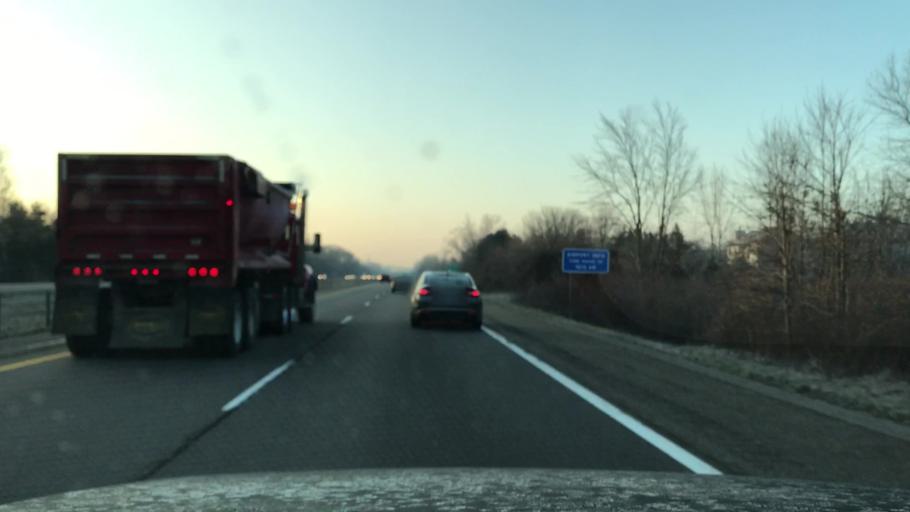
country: US
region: Michigan
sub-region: Kent County
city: East Grand Rapids
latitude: 42.9273
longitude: -85.5576
